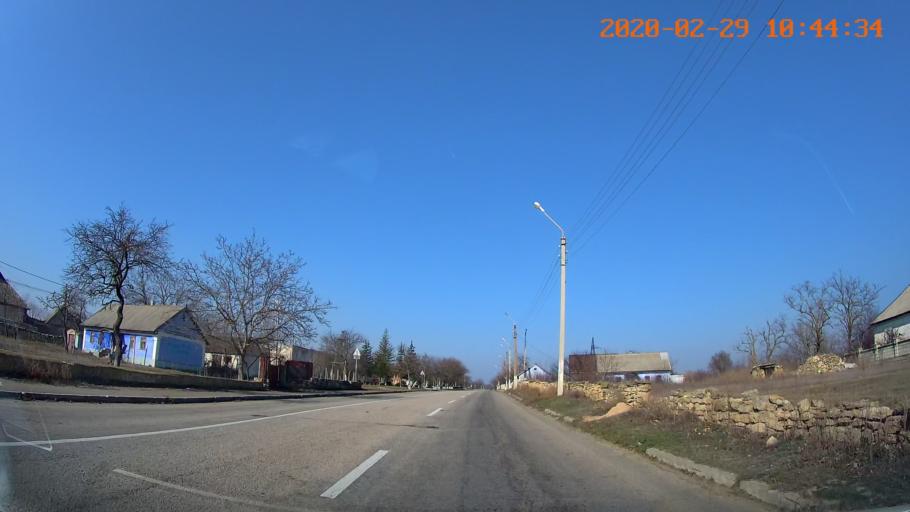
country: MD
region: Telenesti
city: Grigoriopol
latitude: 47.0709
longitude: 29.3932
